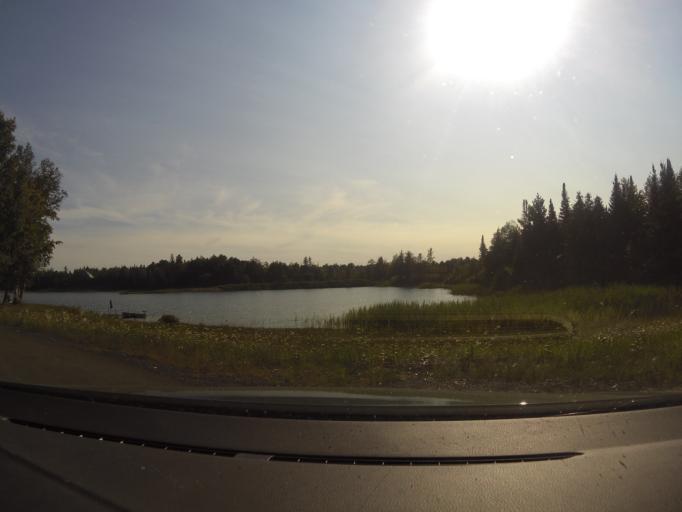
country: CA
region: Ontario
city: Carleton Place
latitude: 45.2802
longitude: -76.0769
